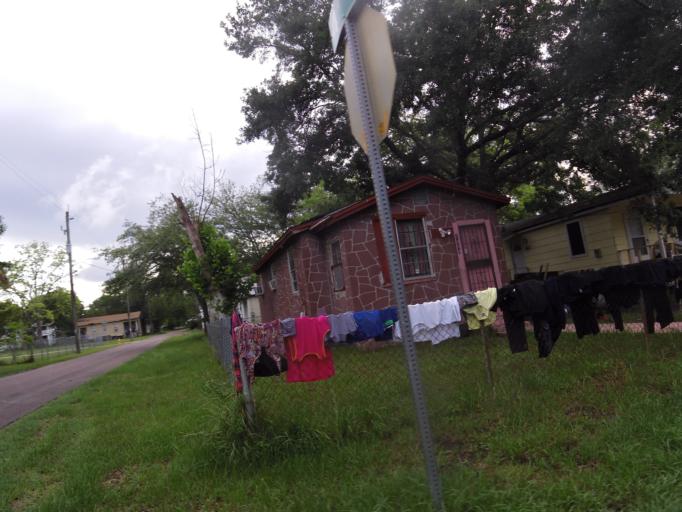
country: US
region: Florida
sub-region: Duval County
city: Jacksonville
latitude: 30.3416
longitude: -81.6693
